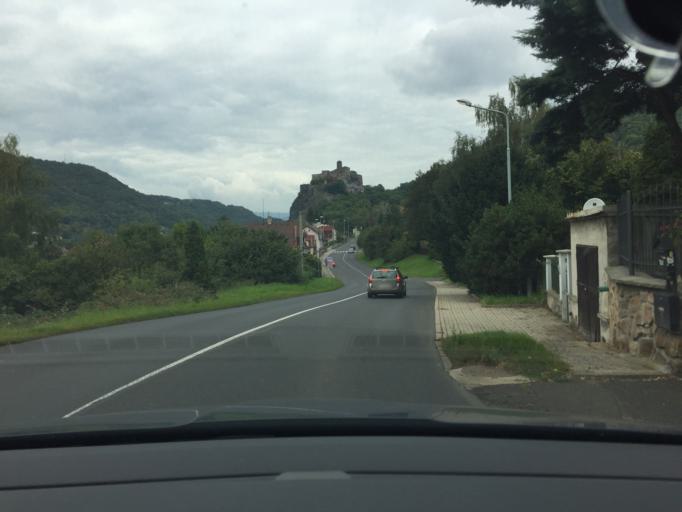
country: CZ
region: Ustecky
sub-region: Okres Usti nad Labem
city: Usti nad Labem
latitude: 50.6327
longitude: 14.0543
